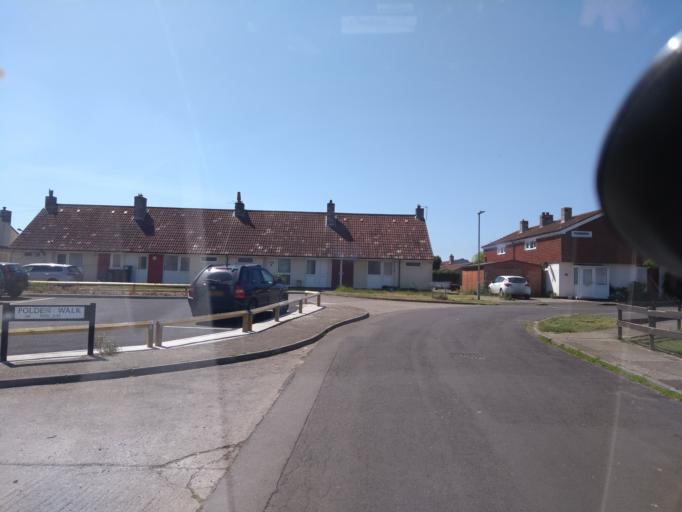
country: GB
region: England
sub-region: Somerset
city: Woolavington
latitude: 51.1633
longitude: -2.9389
